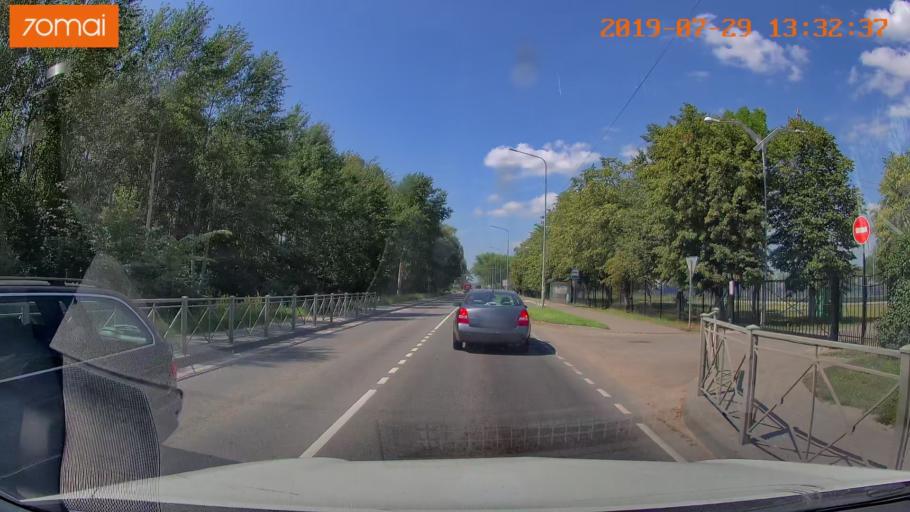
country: RU
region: Kaliningrad
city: Vzmorye
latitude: 54.6979
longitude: 20.2336
